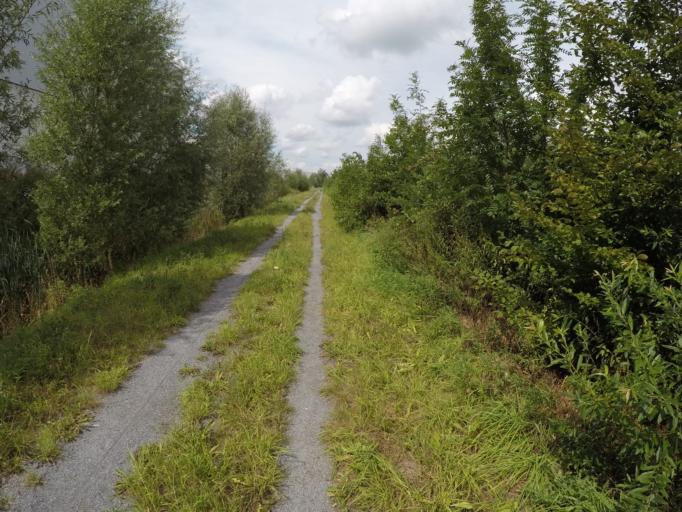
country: BE
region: Flanders
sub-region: Provincie Antwerpen
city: Lier
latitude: 51.1497
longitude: 4.5440
